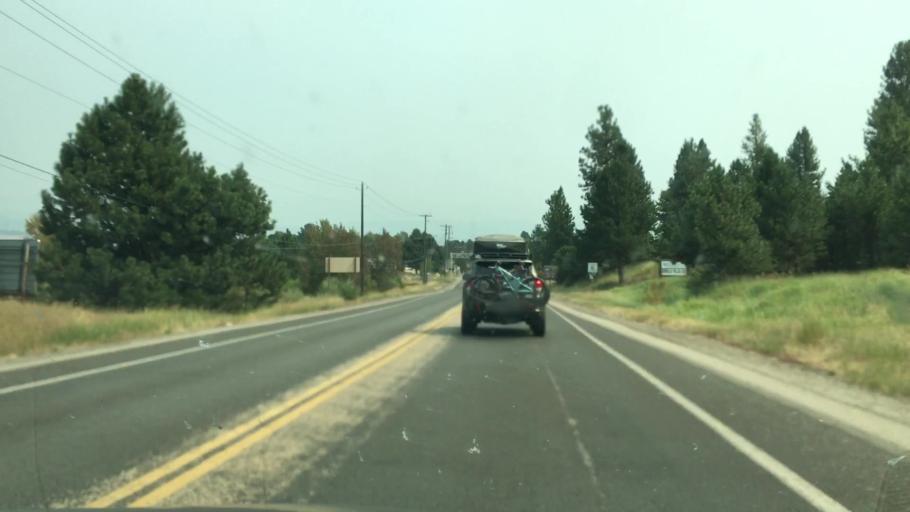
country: US
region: Idaho
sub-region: Valley County
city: Cascade
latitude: 44.5084
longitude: -116.0339
